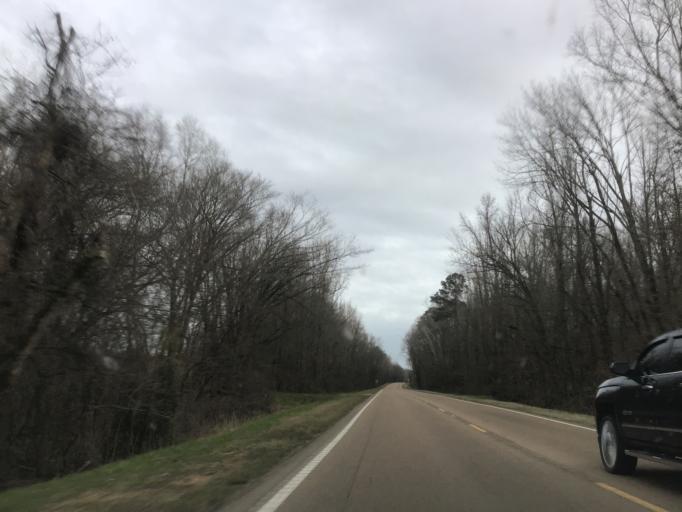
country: US
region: Mississippi
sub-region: Warren County
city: Beechwood
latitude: 32.3096
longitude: -90.8062
